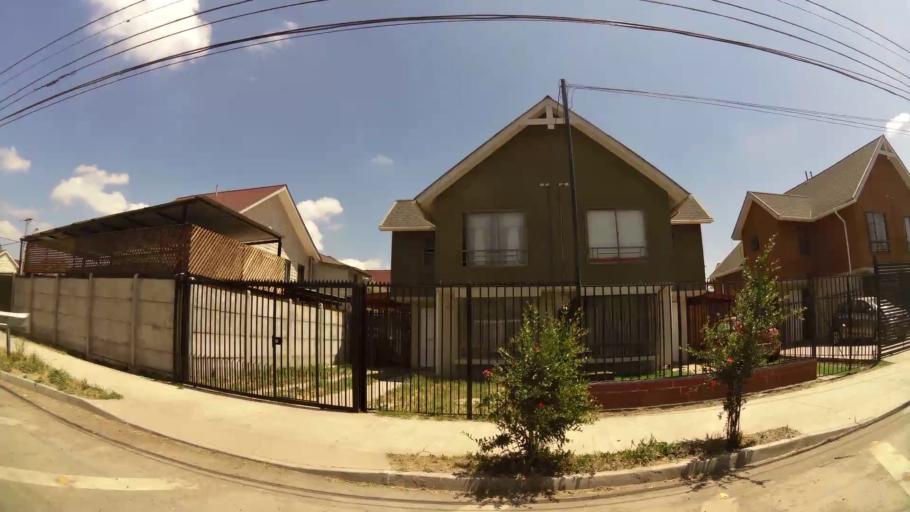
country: CL
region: Santiago Metropolitan
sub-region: Provincia de Talagante
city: Penaflor
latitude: -33.5689
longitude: -70.7950
